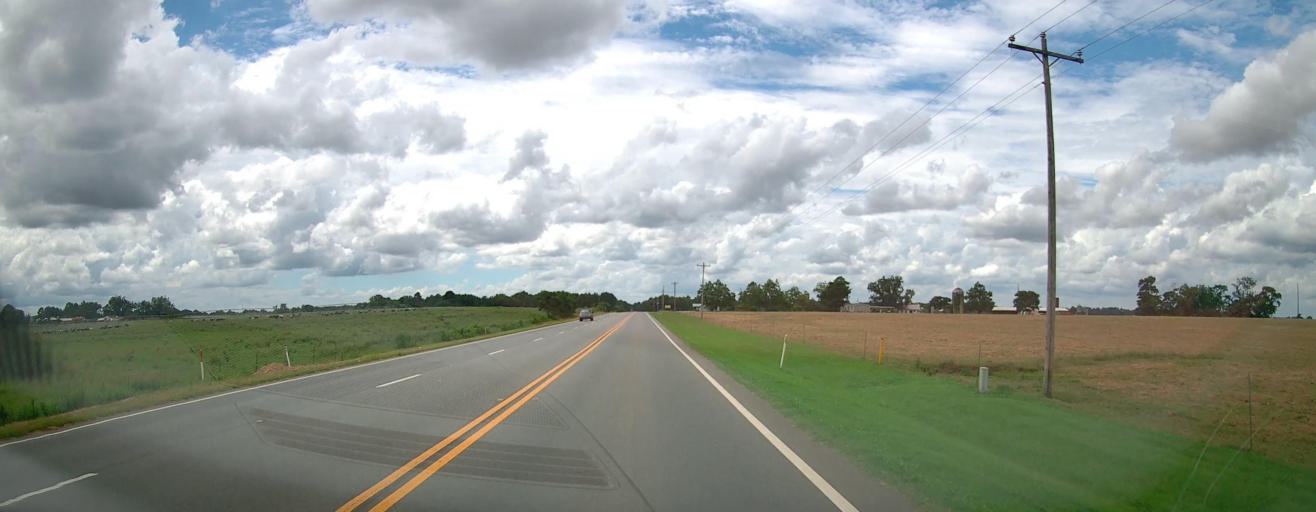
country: US
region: Georgia
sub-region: Macon County
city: Montezuma
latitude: 32.2921
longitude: -83.9310
